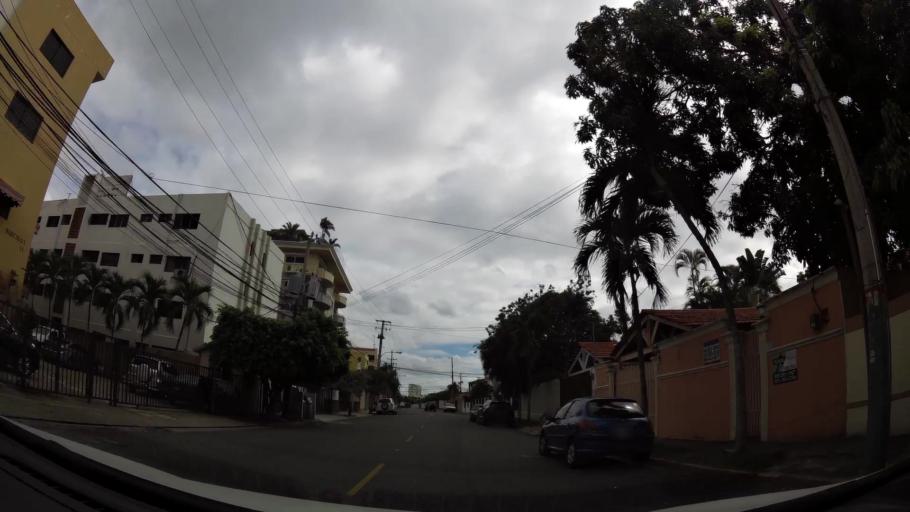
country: DO
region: Nacional
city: Bella Vista
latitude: 18.4519
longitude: -69.9434
